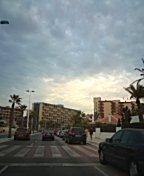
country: ES
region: Murcia
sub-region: Murcia
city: La Manga del Mar Menor
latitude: 37.6836
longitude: -0.7348
